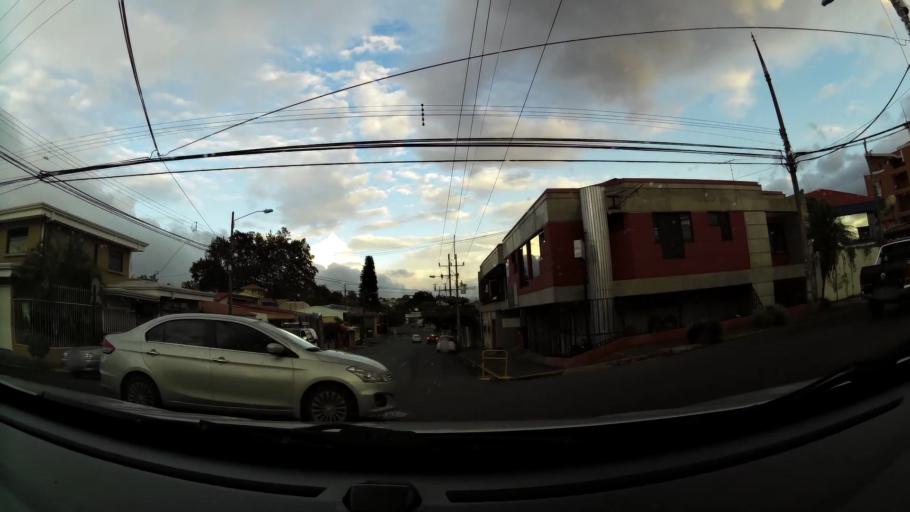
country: CR
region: Heredia
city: Heredia
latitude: 10.0027
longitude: -84.1135
